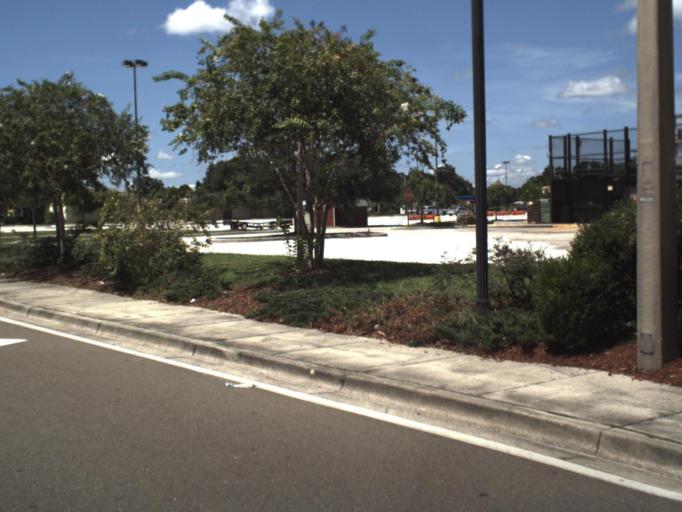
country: US
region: Florida
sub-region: Polk County
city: Winter Haven
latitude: 28.0441
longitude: -81.7331
